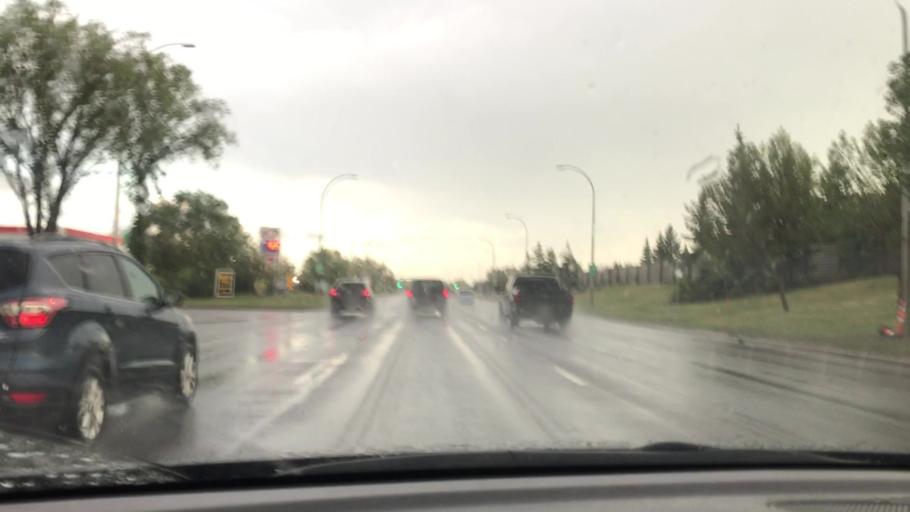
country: CA
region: Alberta
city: Edmonton
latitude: 53.4706
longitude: -113.4957
